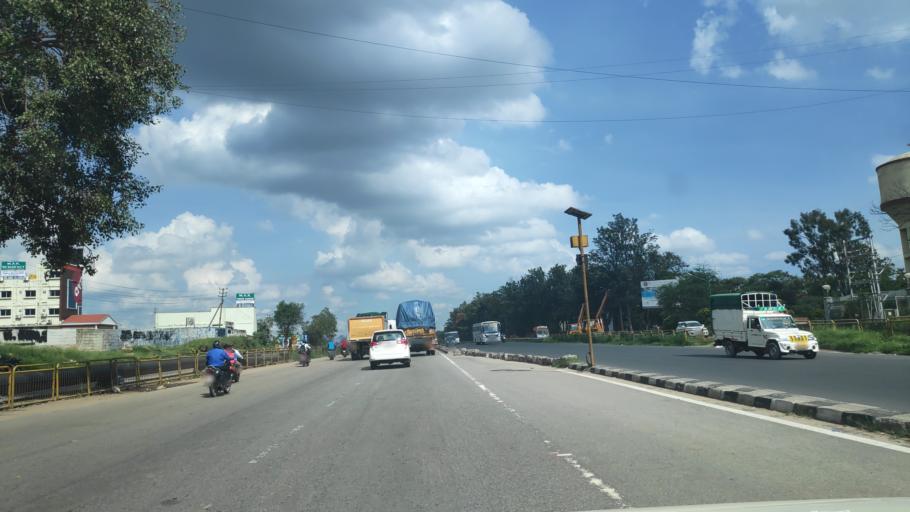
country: IN
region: Karnataka
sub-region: Bangalore Urban
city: Anekal
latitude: 12.7863
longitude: 77.7422
